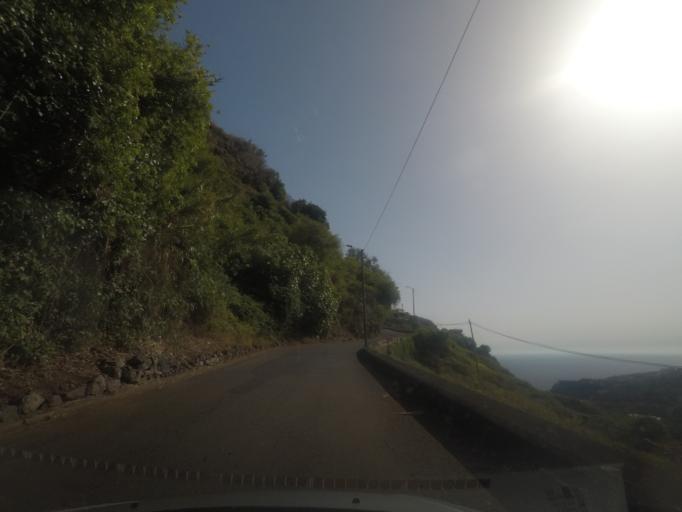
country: PT
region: Madeira
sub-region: Calheta
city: Arco da Calheta
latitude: 32.7289
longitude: -17.1646
